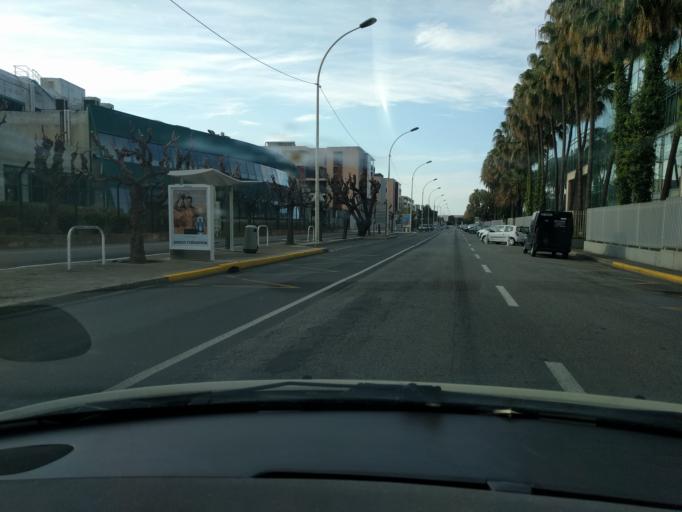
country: FR
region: Provence-Alpes-Cote d'Azur
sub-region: Departement des Alpes-Maritimes
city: Mandelieu-la-Napoule
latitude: 43.5538
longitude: 6.9659
